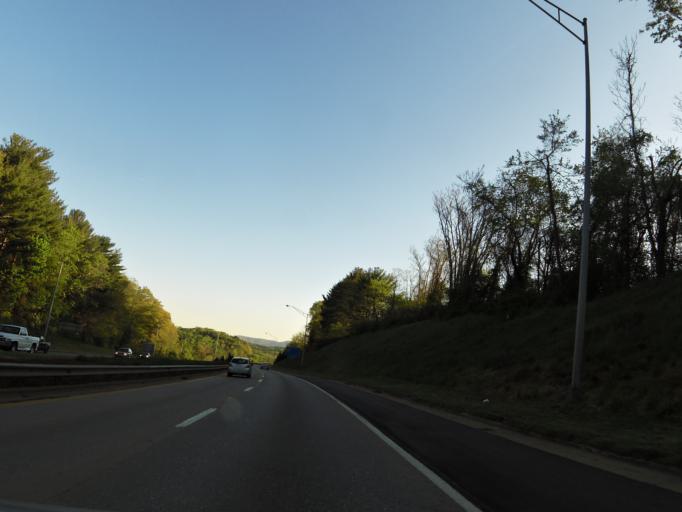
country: US
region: North Carolina
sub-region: Buncombe County
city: Asheville
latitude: 35.5713
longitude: -82.5852
